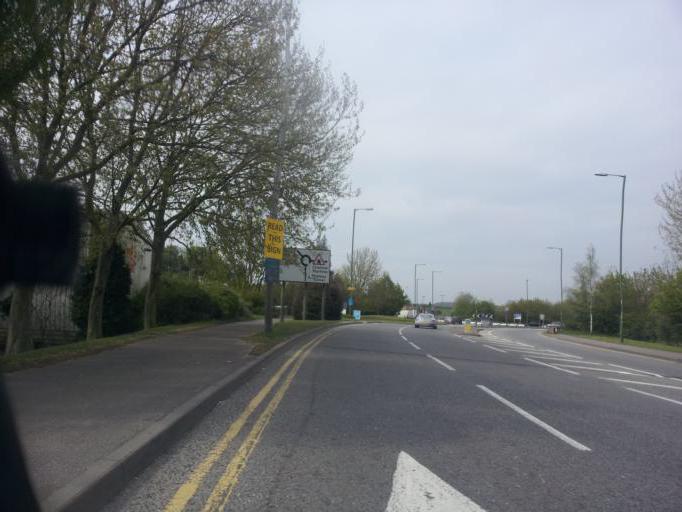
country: GB
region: England
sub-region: Medway
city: Rochester
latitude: 51.4001
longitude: 0.5144
